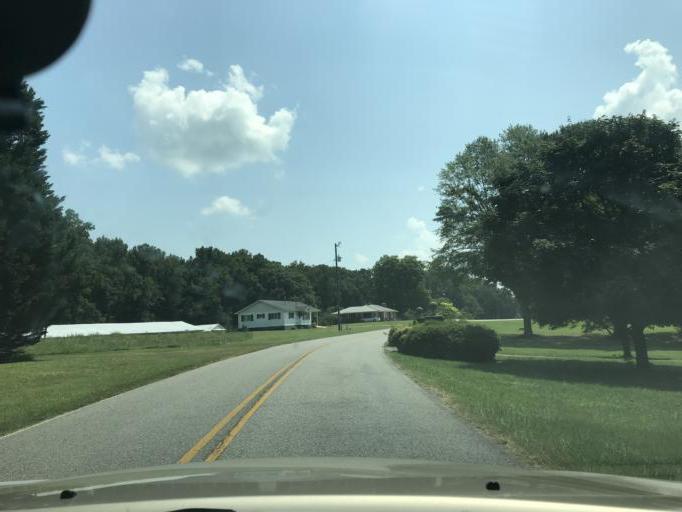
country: US
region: Georgia
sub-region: Dawson County
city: Dawsonville
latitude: 34.3234
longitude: -84.1043
